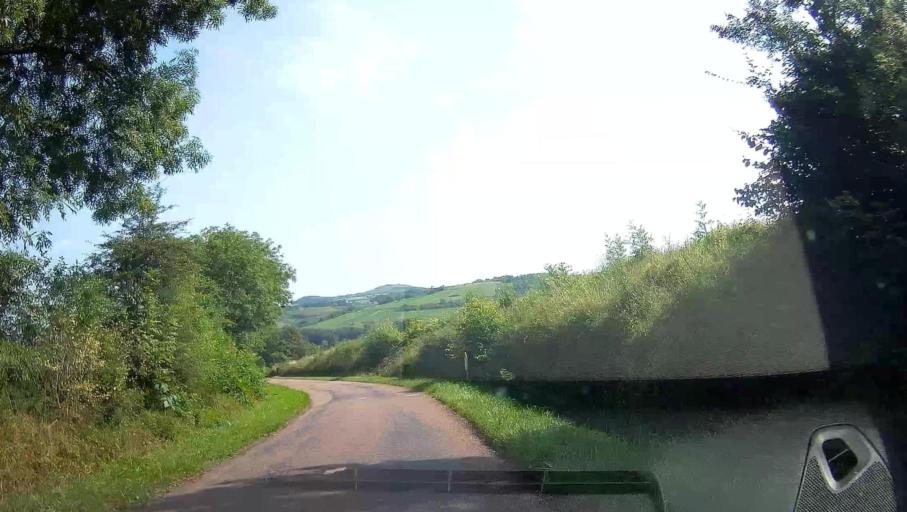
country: FR
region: Bourgogne
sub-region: Departement de la Cote-d'Or
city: Nolay
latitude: 46.9100
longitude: 4.6298
